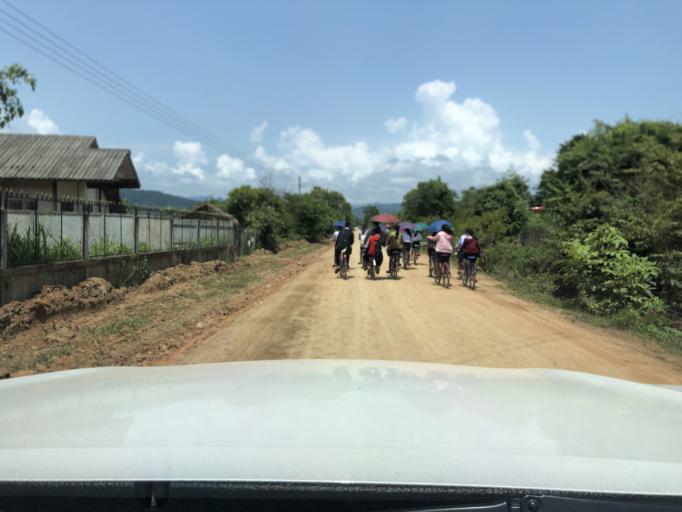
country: LA
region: Xiagnabouli
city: Sainyabuli
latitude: 19.0044
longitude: 101.5138
